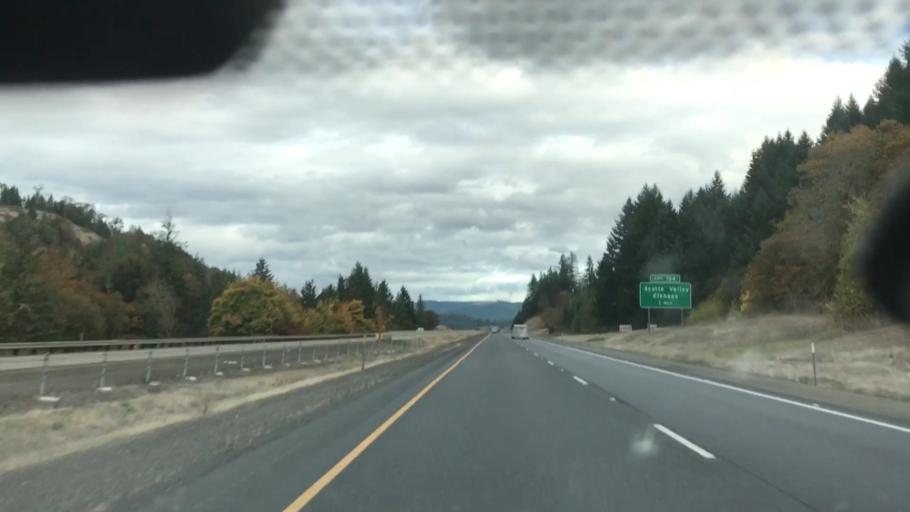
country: US
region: Oregon
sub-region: Douglas County
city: Yoncalla
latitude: 43.5977
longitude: -123.2383
